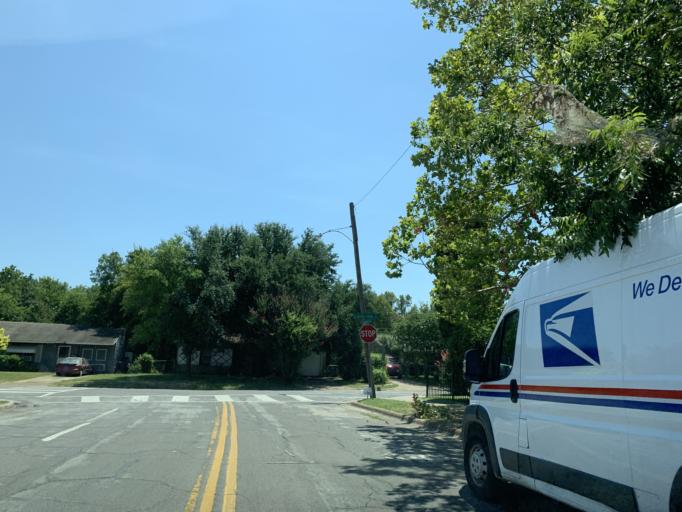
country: US
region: Texas
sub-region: Dallas County
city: Hutchins
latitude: 32.6784
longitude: -96.7627
